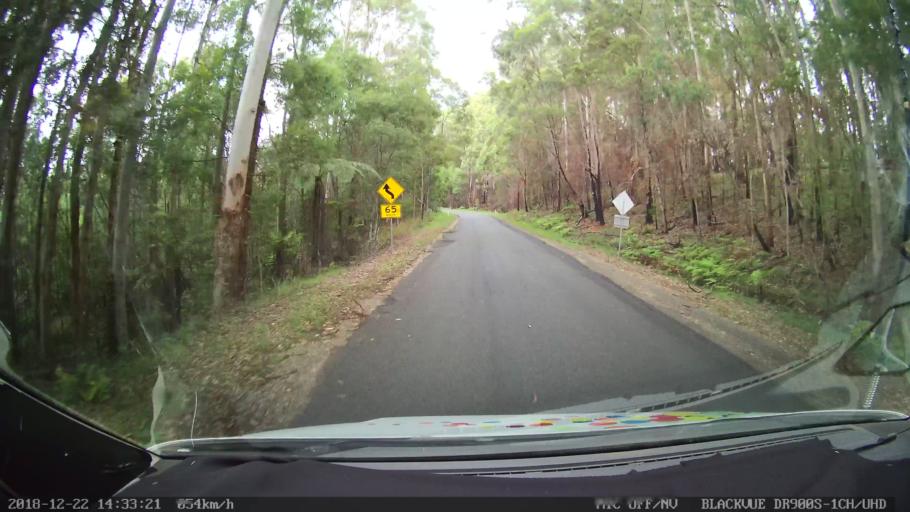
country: AU
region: New South Wales
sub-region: Bellingen
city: Dorrigo
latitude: -30.1120
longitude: 152.6235
